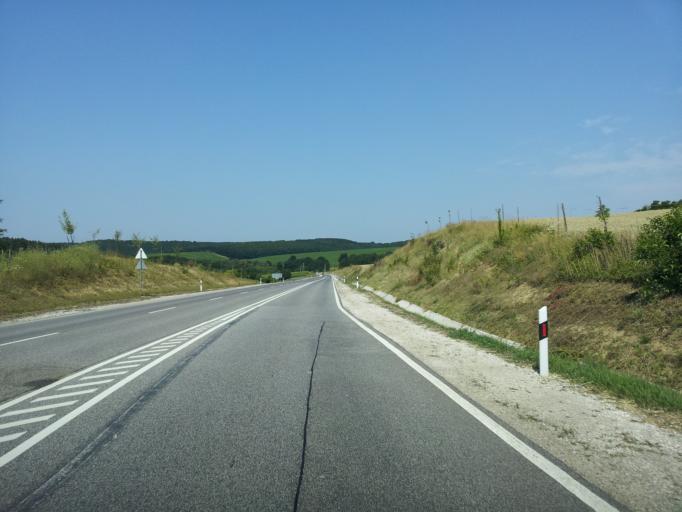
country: HU
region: Zala
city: Zalaszentgrot
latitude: 46.8337
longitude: 17.0424
